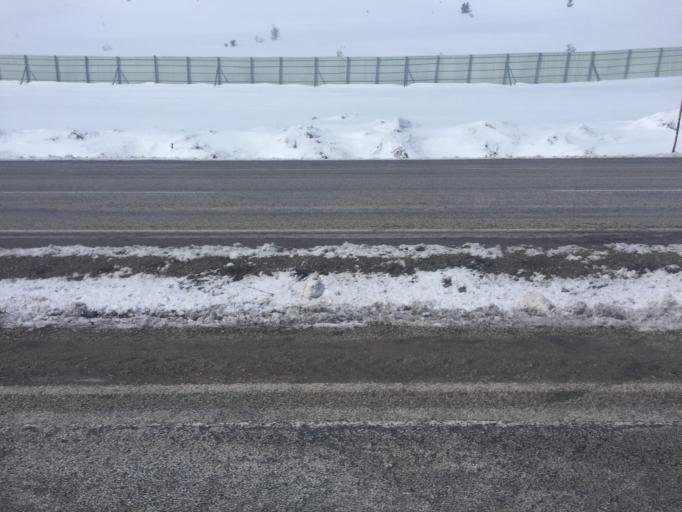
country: TR
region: Kahramanmaras
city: Goksun
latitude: 38.1882
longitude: 36.4568
